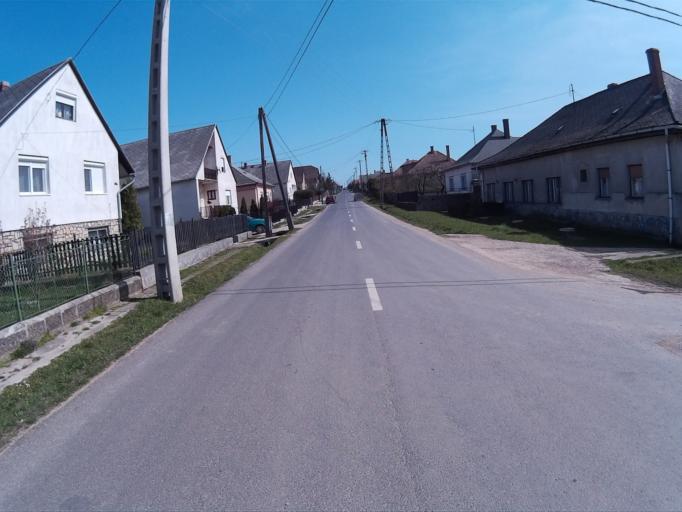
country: HU
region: Veszprem
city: Herend
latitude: 47.1878
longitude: 17.8074
